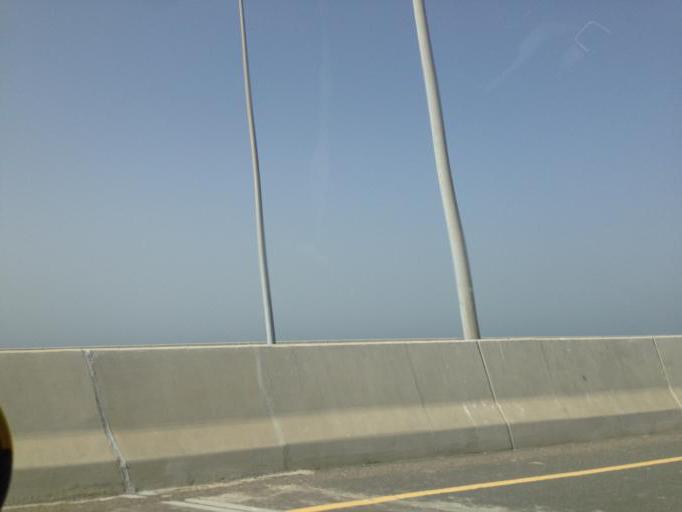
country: OM
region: Al Batinah
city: Barka'
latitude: 23.7069
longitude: 57.9403
